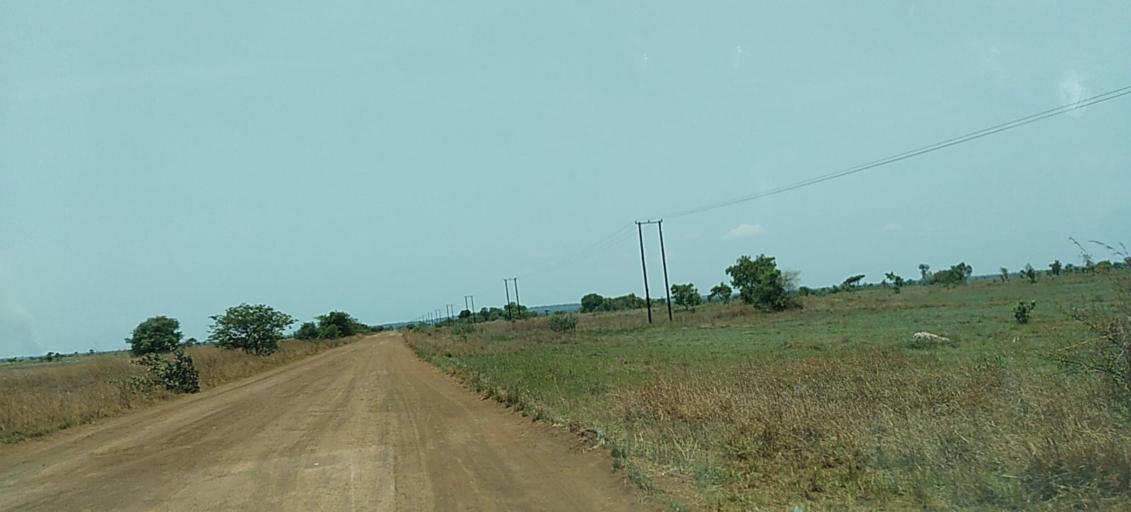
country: ZM
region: Copperbelt
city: Mpongwe
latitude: -13.6698
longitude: 27.8542
